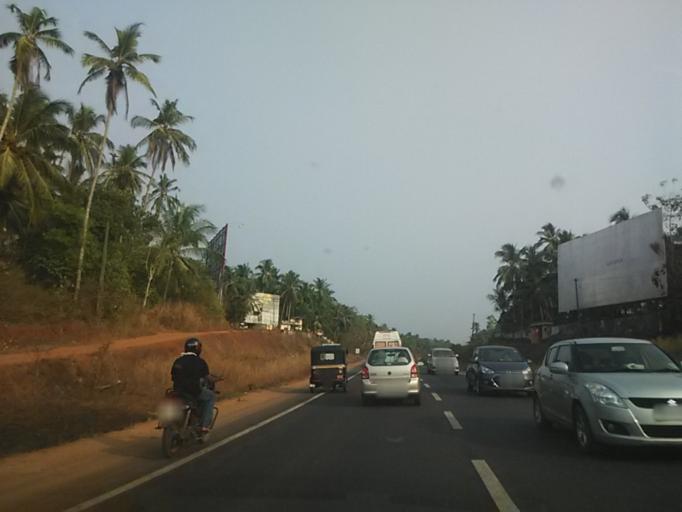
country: IN
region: Kerala
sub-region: Kozhikode
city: Kozhikode
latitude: 11.3079
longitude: 75.7859
